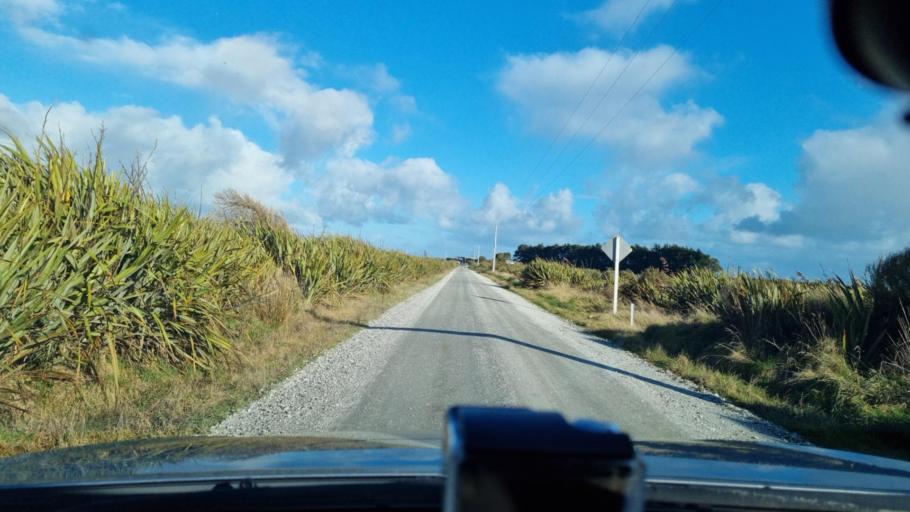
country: NZ
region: Southland
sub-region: Invercargill City
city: Bluff
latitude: -46.5215
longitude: 168.4112
